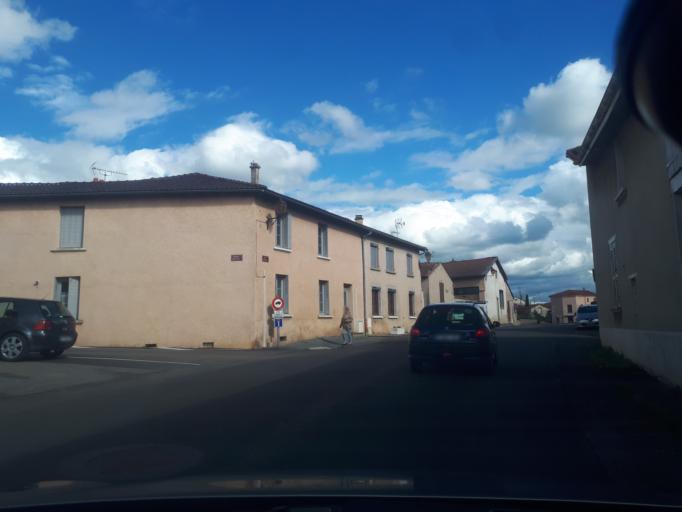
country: FR
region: Rhone-Alpes
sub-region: Departement de la Loire
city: Pouilly-les-Feurs
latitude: 45.7993
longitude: 4.2310
